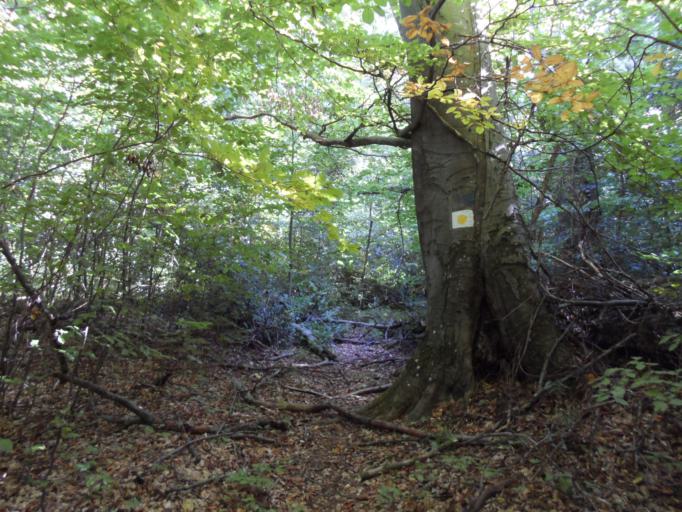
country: HU
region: Veszprem
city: Zirc
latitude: 47.2816
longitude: 17.7651
